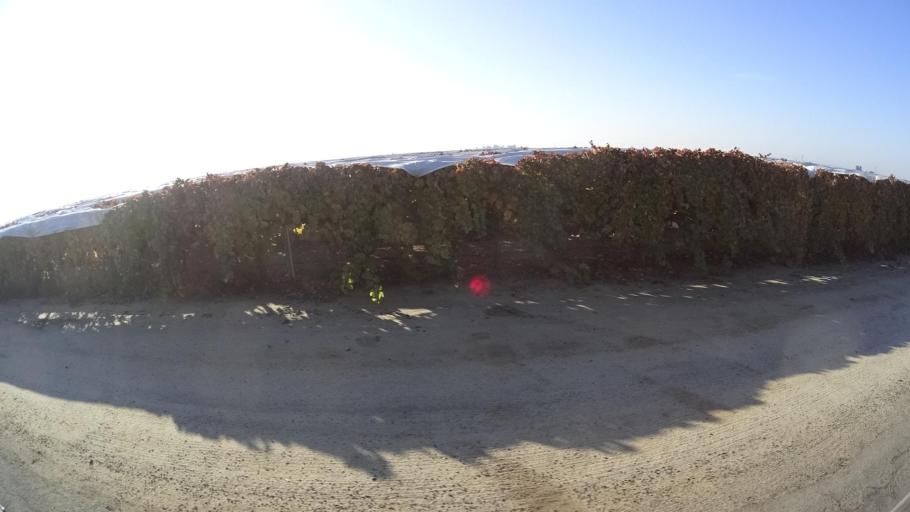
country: US
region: California
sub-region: Tulare County
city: Richgrove
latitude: 35.7687
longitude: -119.1726
